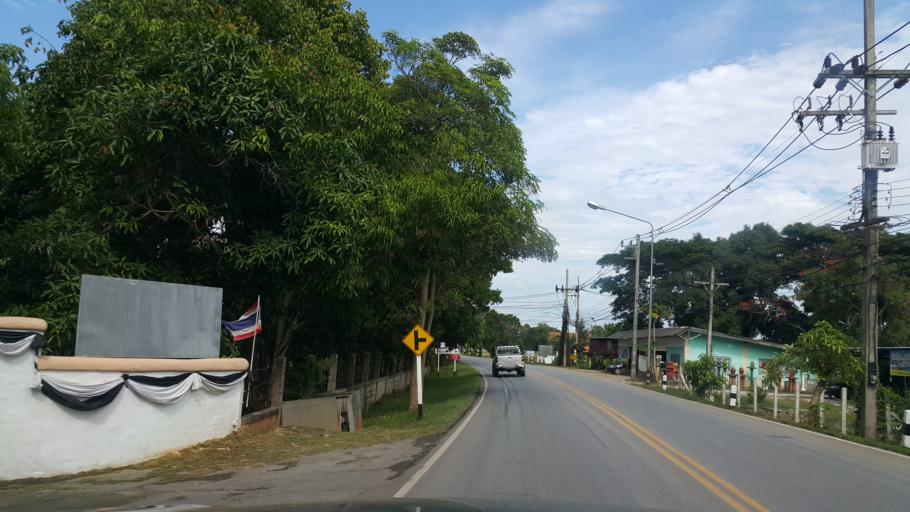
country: TH
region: Chiang Rai
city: Chiang Rai
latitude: 19.9125
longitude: 99.8723
